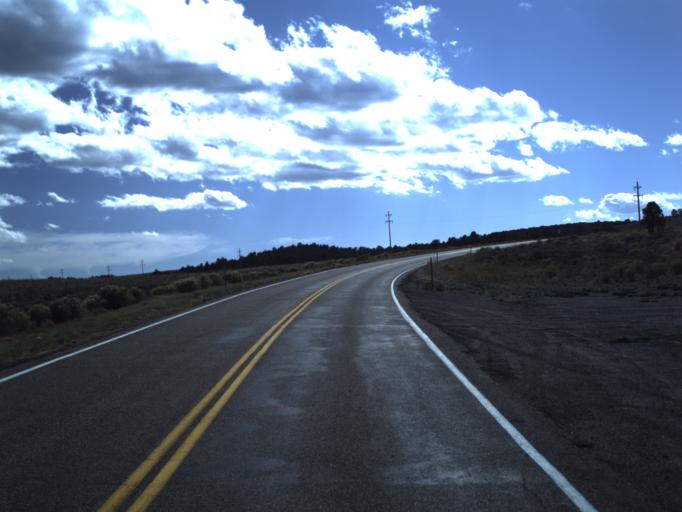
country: US
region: Utah
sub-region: Garfield County
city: Panguitch
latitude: 37.7737
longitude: -112.4443
